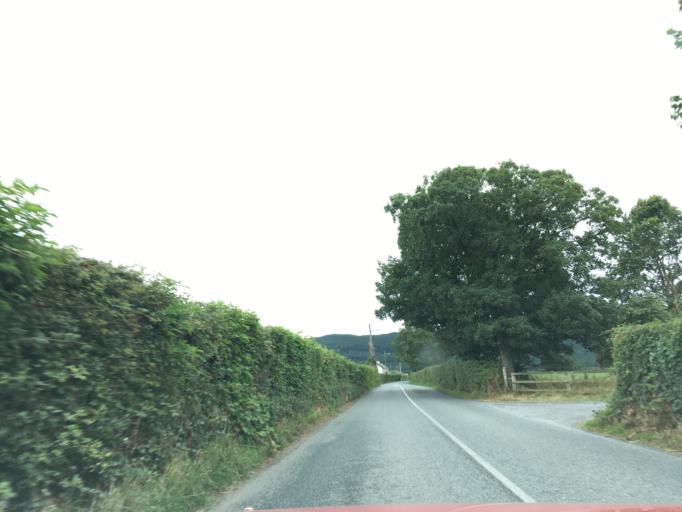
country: IE
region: Munster
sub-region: South Tipperary
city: Cluain Meala
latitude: 52.3722
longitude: -7.5879
